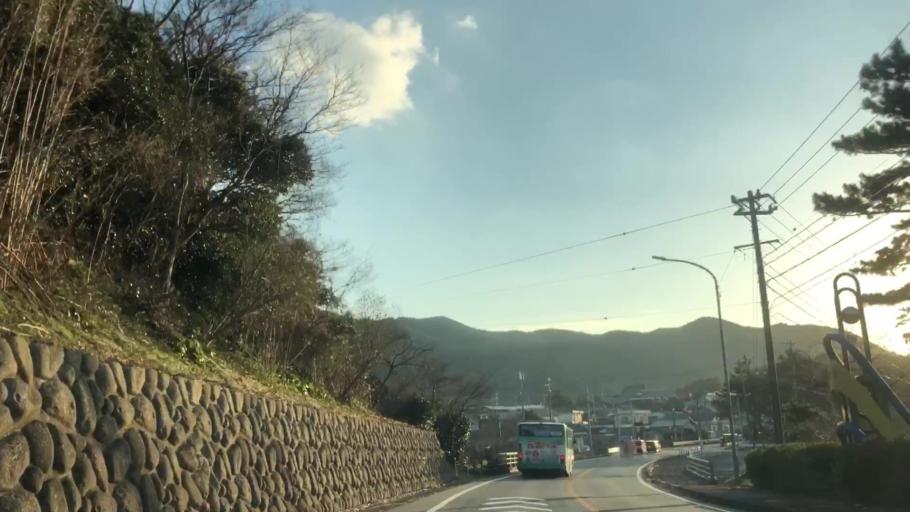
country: JP
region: Aichi
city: Tahara
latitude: 34.6602
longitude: 137.1786
